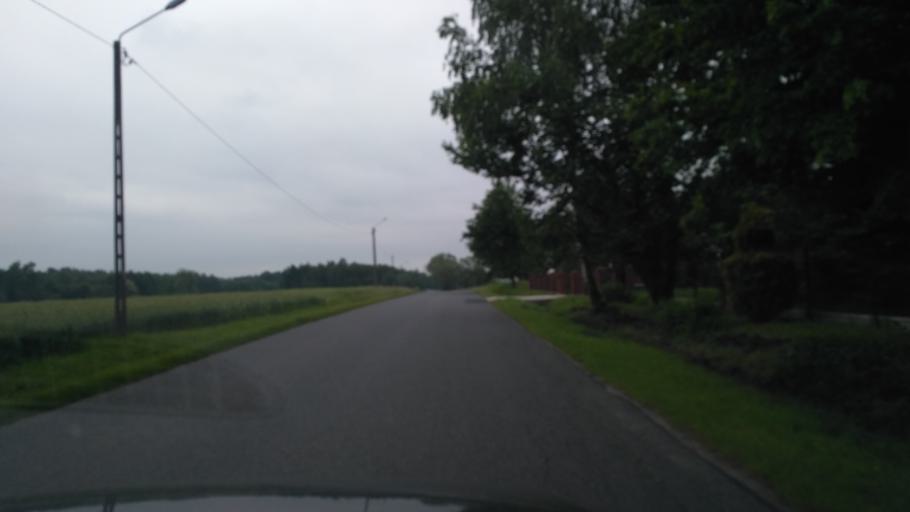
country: PL
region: Subcarpathian Voivodeship
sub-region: Powiat kolbuszowski
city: Niwiska
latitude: 50.1717
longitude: 21.6679
